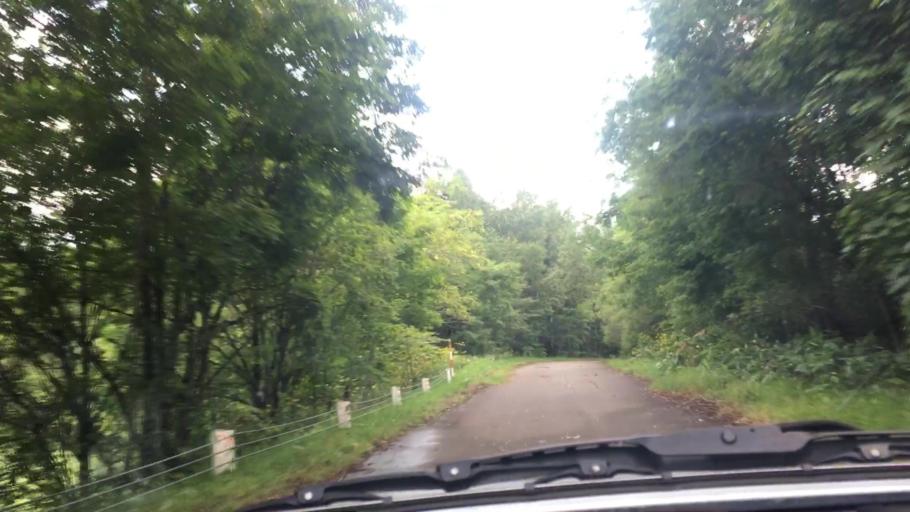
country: JP
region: Hokkaido
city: Shimo-furano
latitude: 43.0110
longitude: 142.4166
